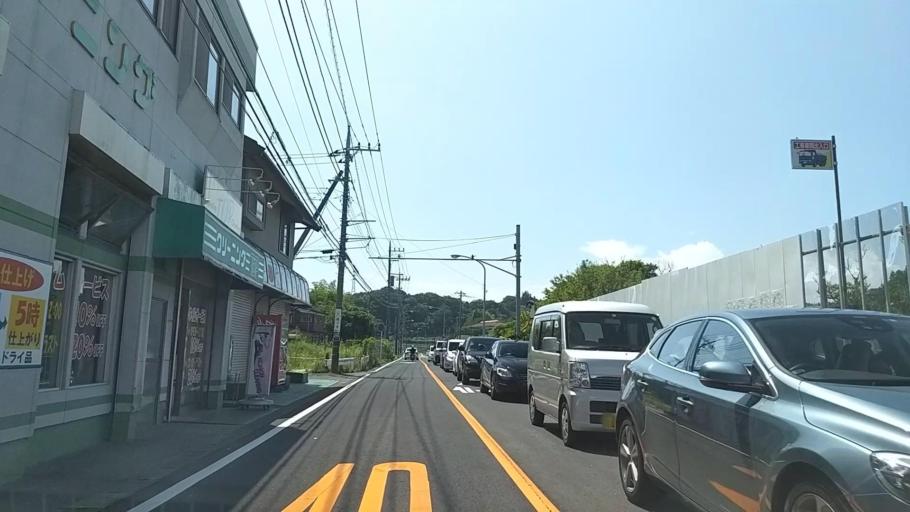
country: JP
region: Kanagawa
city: Fujisawa
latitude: 35.3645
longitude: 139.5207
